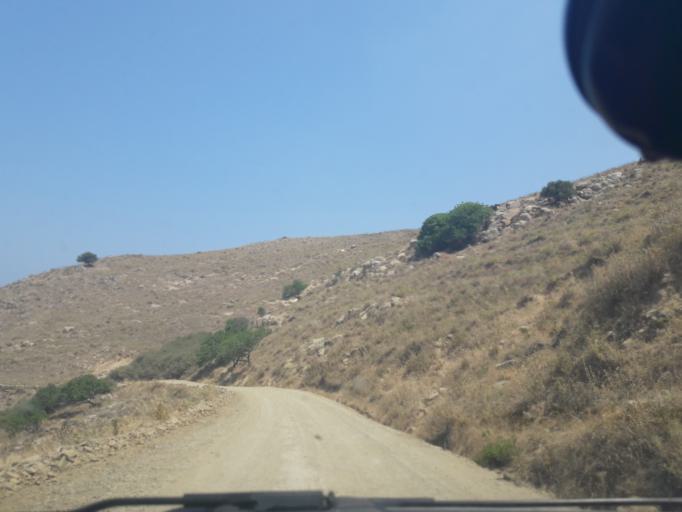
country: GR
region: North Aegean
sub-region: Nomos Lesvou
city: Myrina
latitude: 39.9726
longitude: 25.1525
